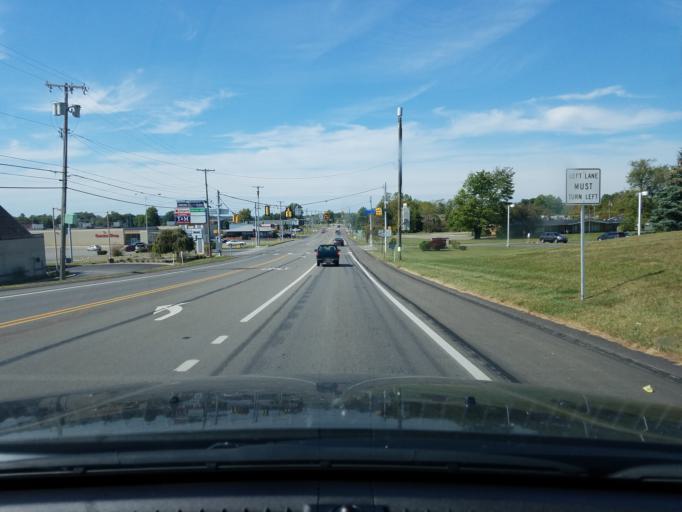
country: US
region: Pennsylvania
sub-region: Lawrence County
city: New Castle
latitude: 40.9646
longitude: -80.3059
